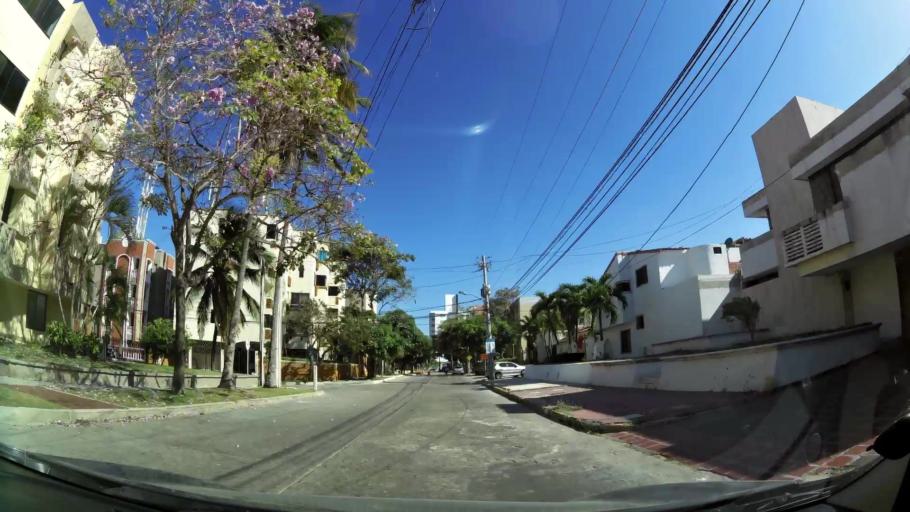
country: CO
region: Atlantico
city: Barranquilla
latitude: 11.0174
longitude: -74.8171
